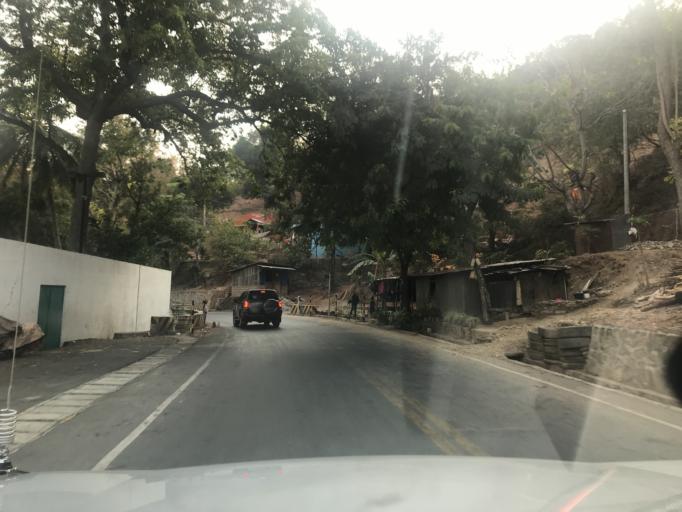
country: TL
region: Dili
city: Dili
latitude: -8.5745
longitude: 125.5854
